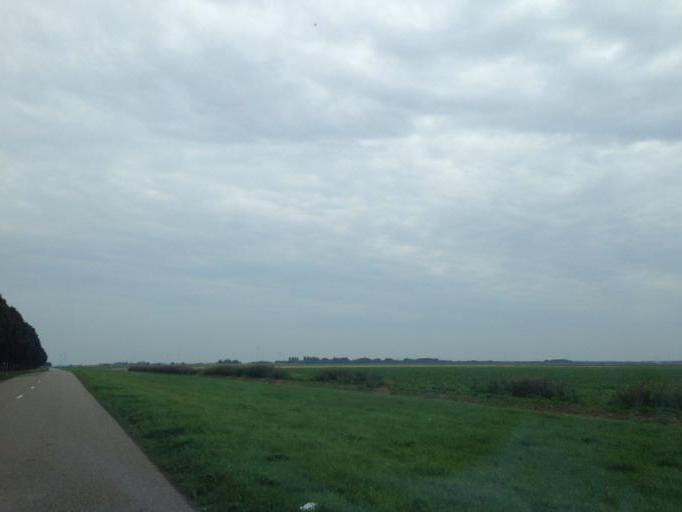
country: NL
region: Flevoland
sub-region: Gemeente Almere
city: Almere Stad
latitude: 52.3861
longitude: 5.3314
